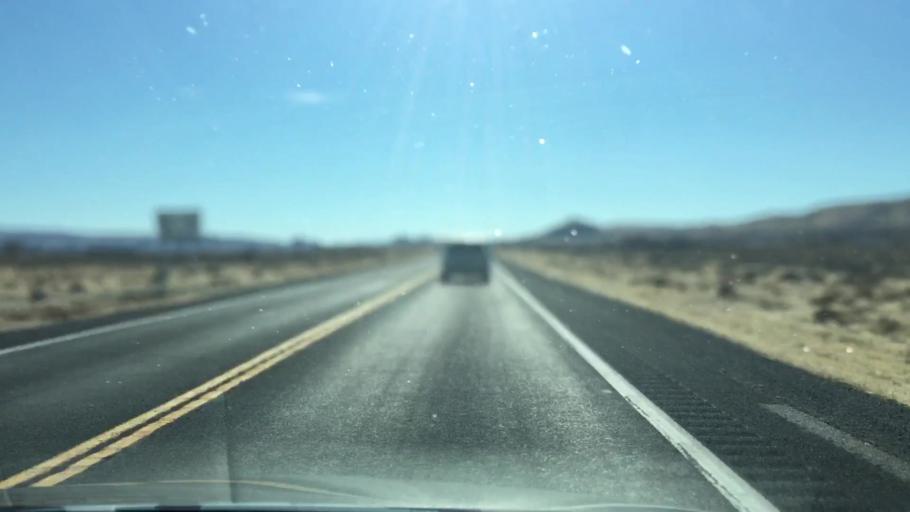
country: US
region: Nevada
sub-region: Lyon County
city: Silver Springs
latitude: 39.3725
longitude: -119.2342
